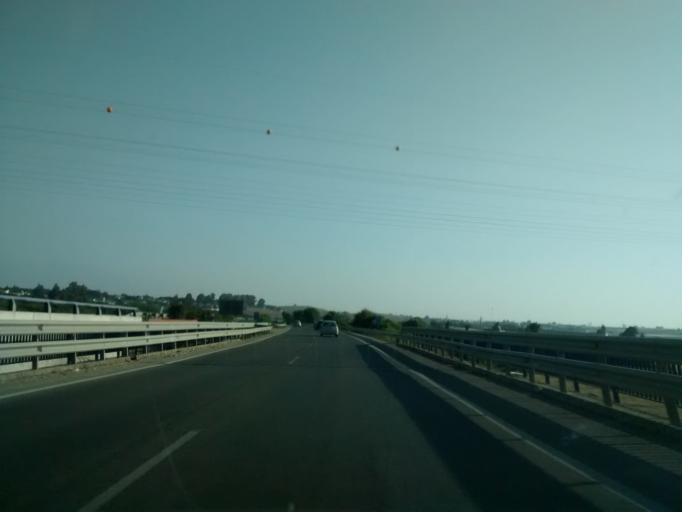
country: ES
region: Andalusia
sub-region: Provincia de Cadiz
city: Chiclana de la Frontera
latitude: 36.4157
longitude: -6.1187
